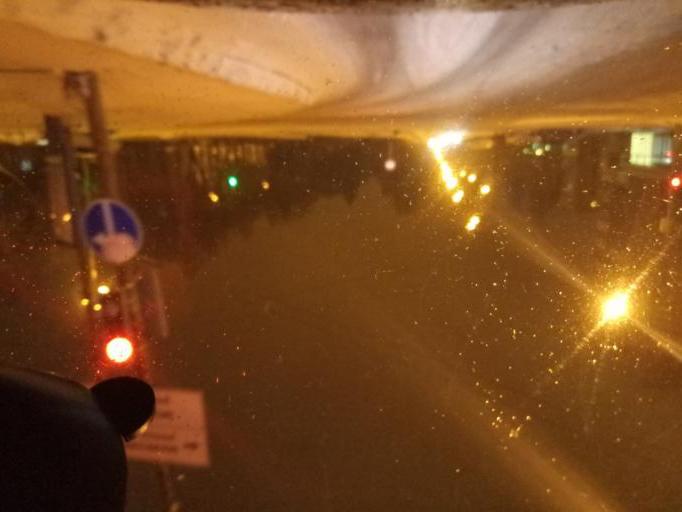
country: RU
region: Tula
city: Novomoskovsk
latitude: 54.0044
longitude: 38.2960
